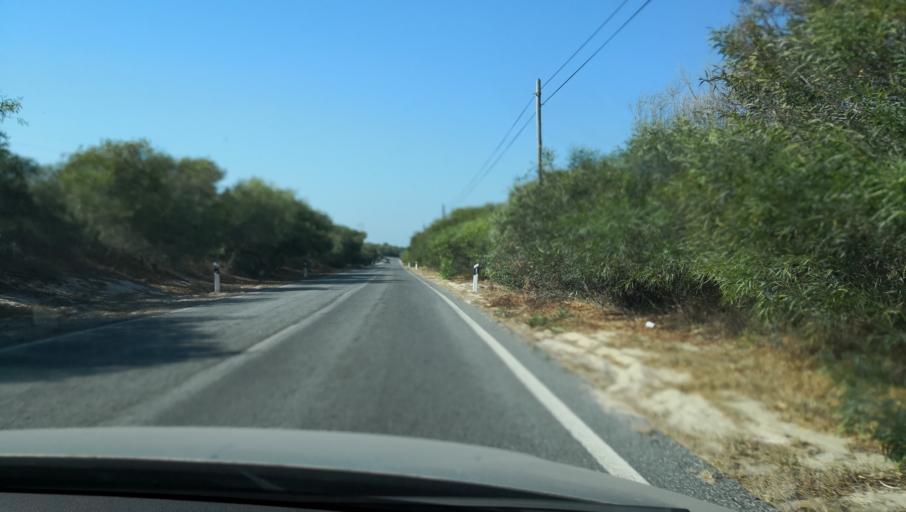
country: PT
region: Setubal
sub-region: Setubal
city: Setubal
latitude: 38.4083
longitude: -8.8112
